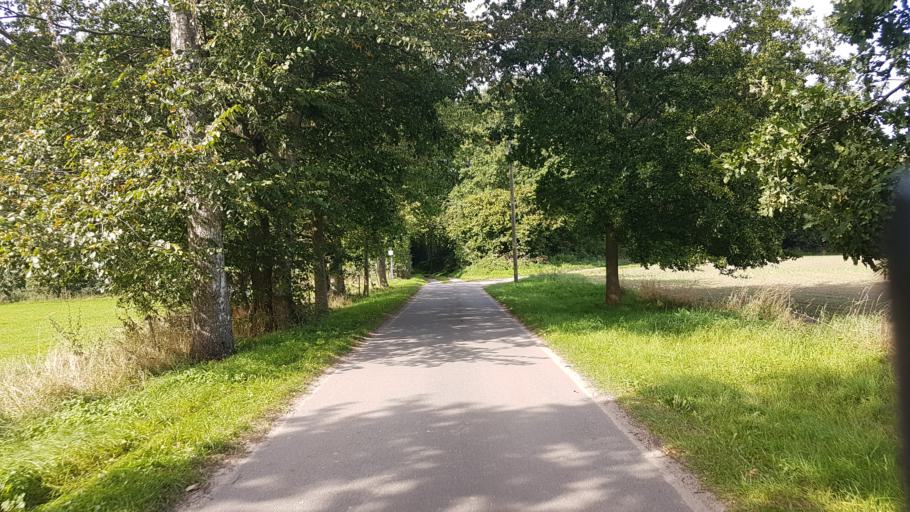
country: DE
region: Mecklenburg-Vorpommern
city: Samtens
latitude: 54.3887
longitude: 13.2655
